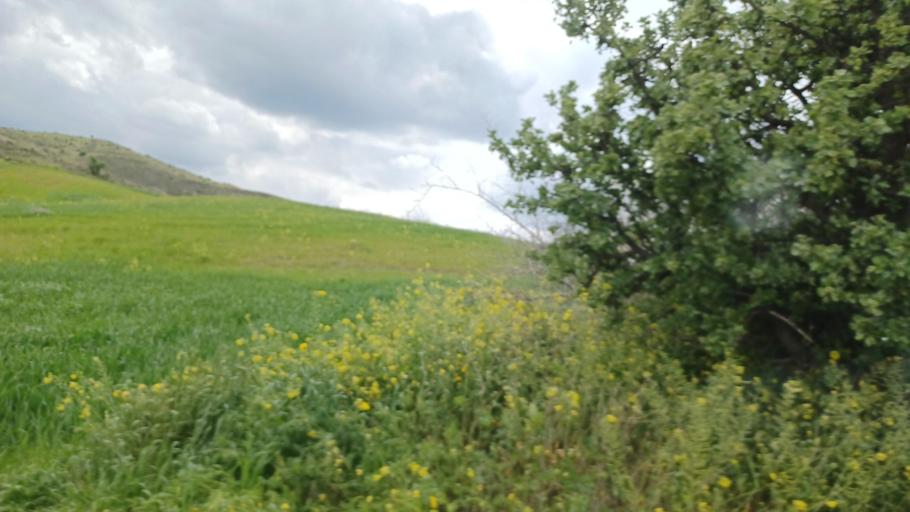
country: CY
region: Lefkosia
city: Lefka
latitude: 35.0871
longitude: 32.9304
